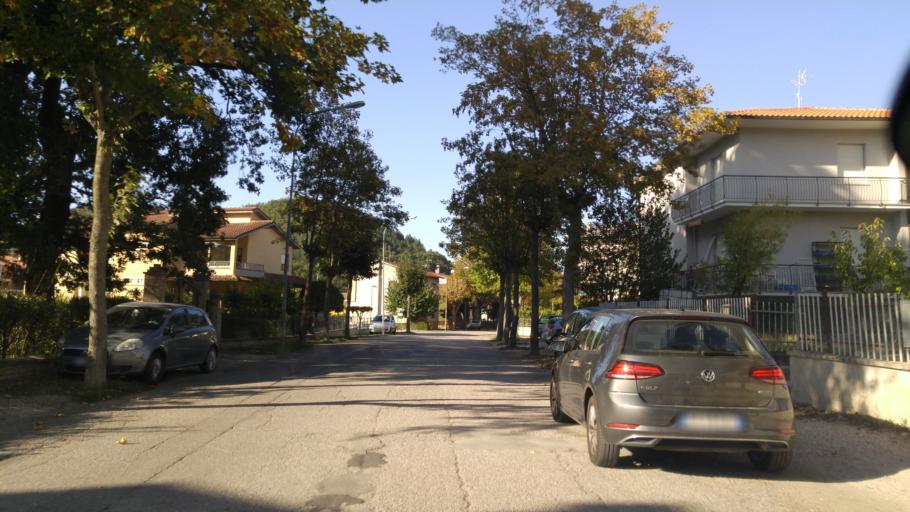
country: IT
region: The Marches
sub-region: Provincia di Pesaro e Urbino
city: Fermignano
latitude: 43.6695
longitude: 12.6440
